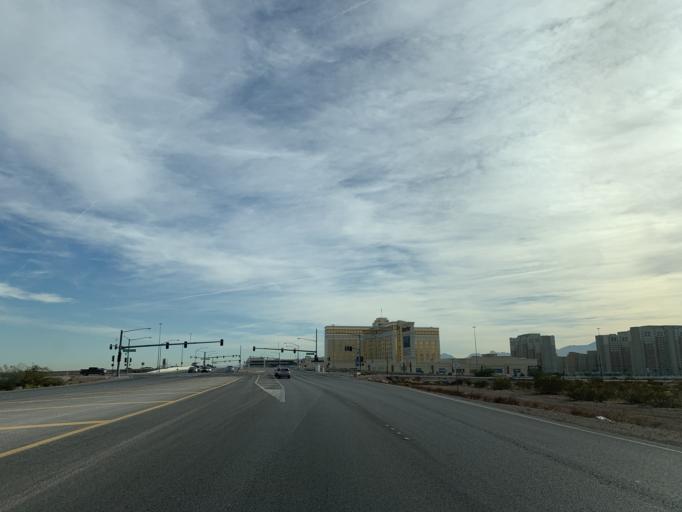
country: US
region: Nevada
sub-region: Clark County
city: Enterprise
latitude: 36.0130
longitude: -115.1847
